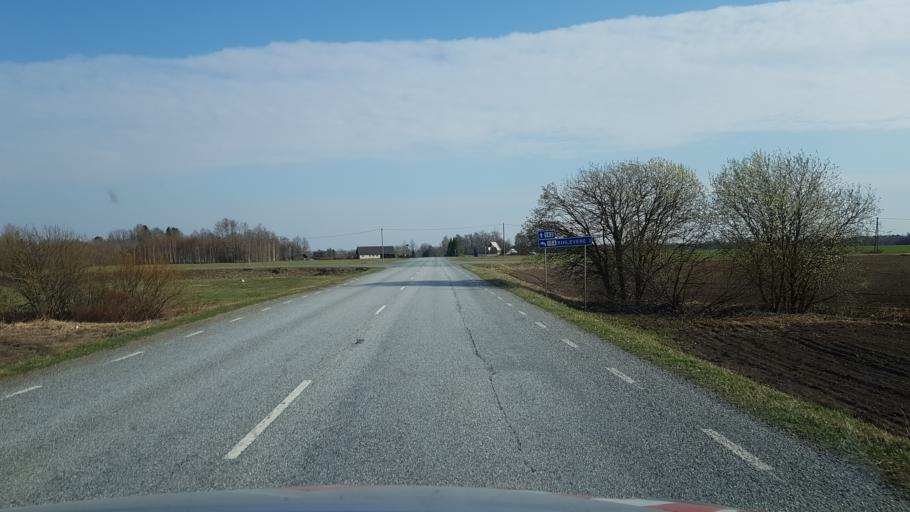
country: EE
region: Laeaene-Virumaa
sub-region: Kadrina vald
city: Kadrina
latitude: 59.3763
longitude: 26.0976
